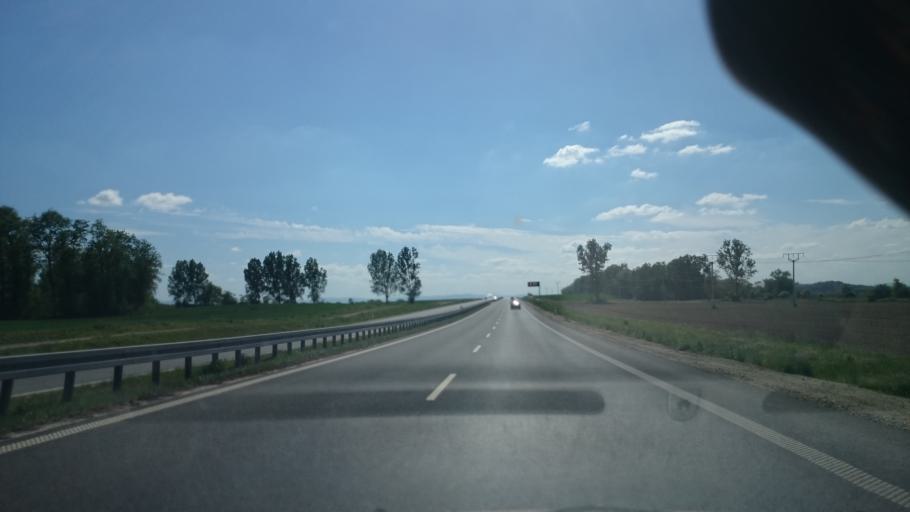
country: PL
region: Opole Voivodeship
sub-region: Powiat nyski
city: Nysa
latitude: 50.4944
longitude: 17.2855
